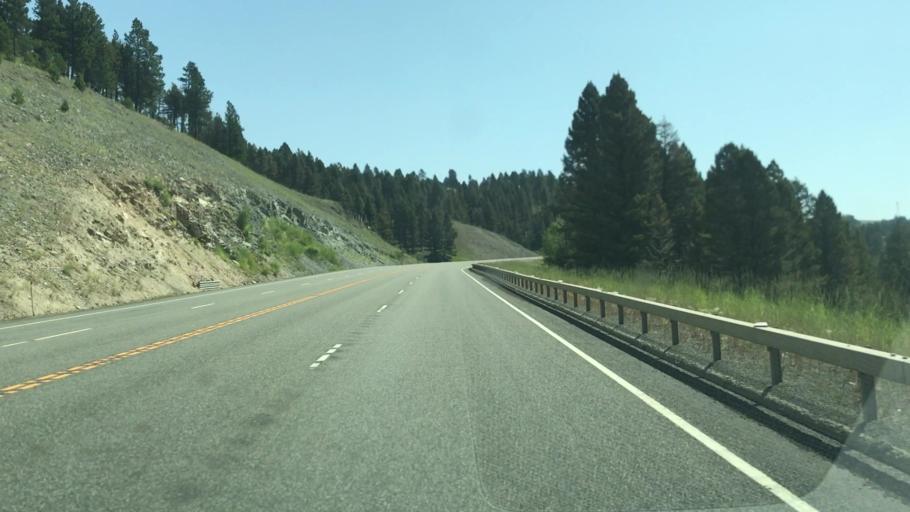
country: US
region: Montana
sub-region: Lewis and Clark County
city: Helena West Side
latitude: 46.5588
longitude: -112.3504
